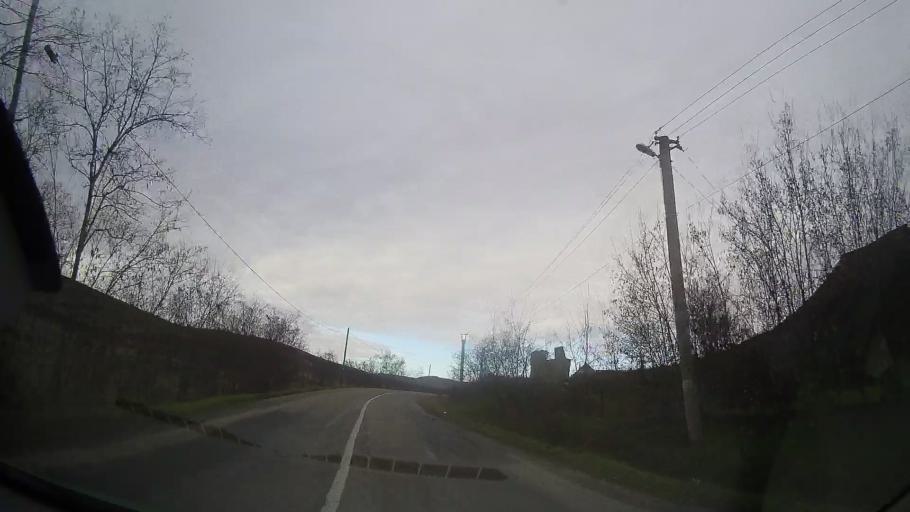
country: RO
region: Cluj
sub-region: Comuna Camarasu
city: Camarasu
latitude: 46.8072
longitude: 24.1448
